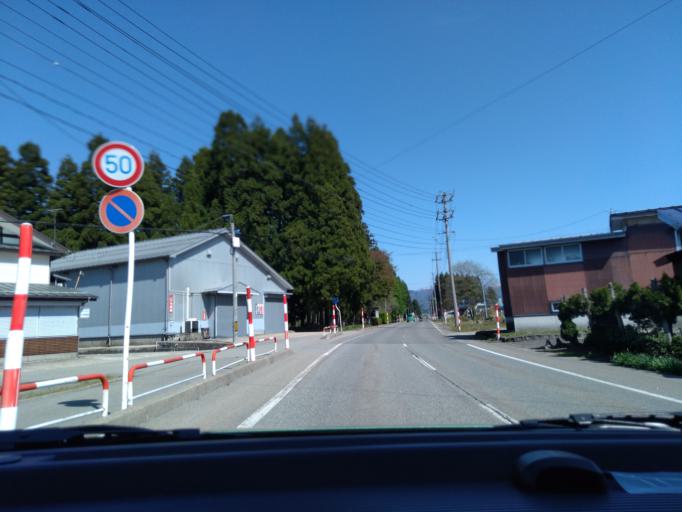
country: JP
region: Akita
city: Kakunodatemachi
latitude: 39.5759
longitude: 140.5686
